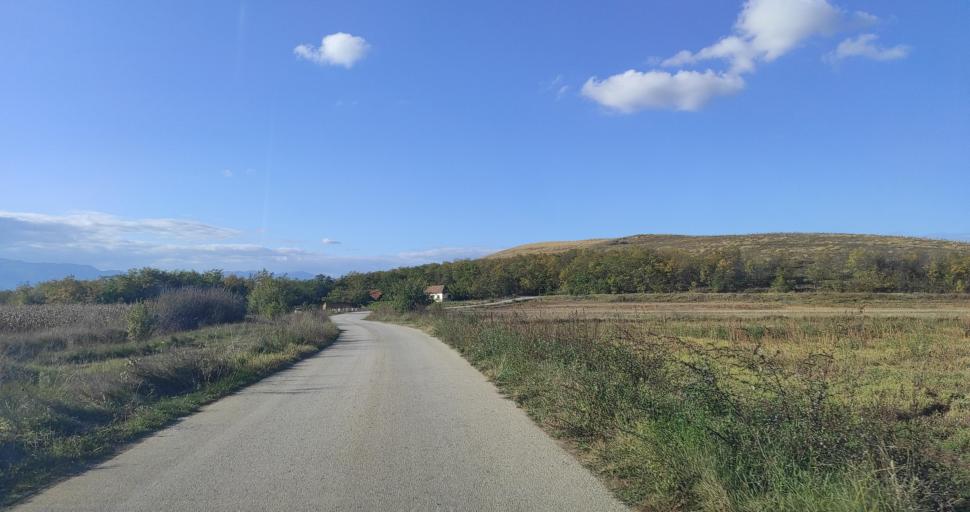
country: MK
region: Prilep
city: Topolcani
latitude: 41.2833
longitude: 21.4212
